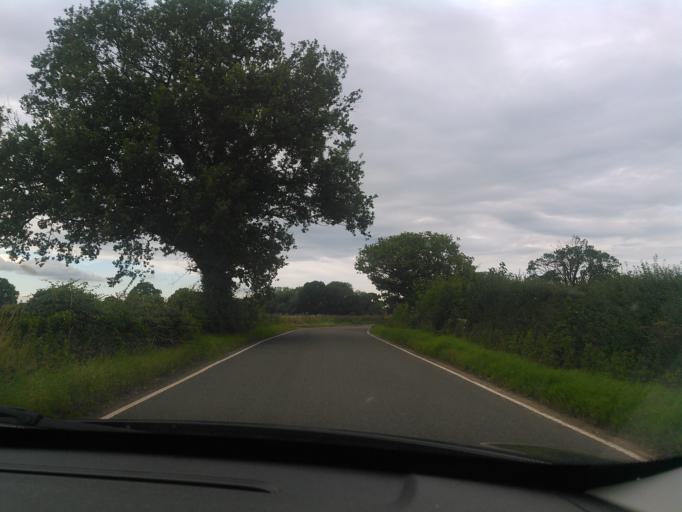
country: GB
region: England
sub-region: Shropshire
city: Prees
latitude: 52.8629
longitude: -2.6648
